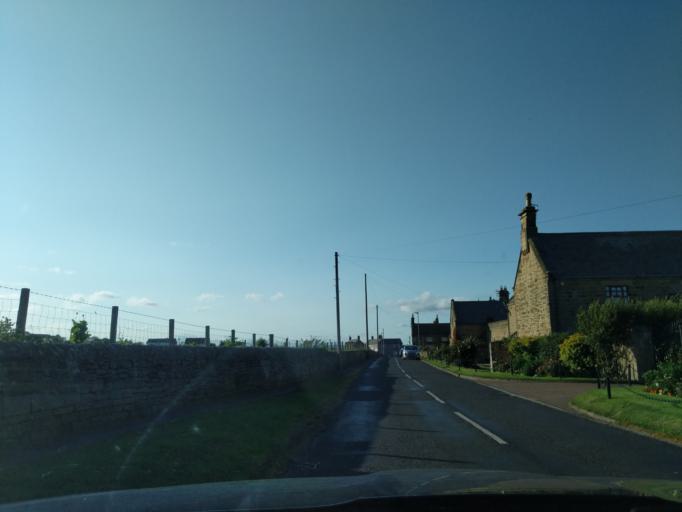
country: GB
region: England
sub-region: Northumberland
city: Lynemouth
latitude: 55.2340
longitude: -1.5361
